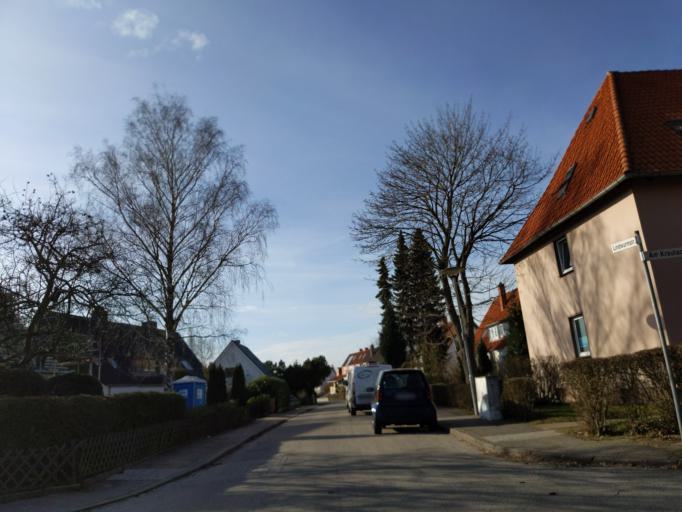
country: DE
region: Schleswig-Holstein
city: Travemuende
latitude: 53.9569
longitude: 10.8454
